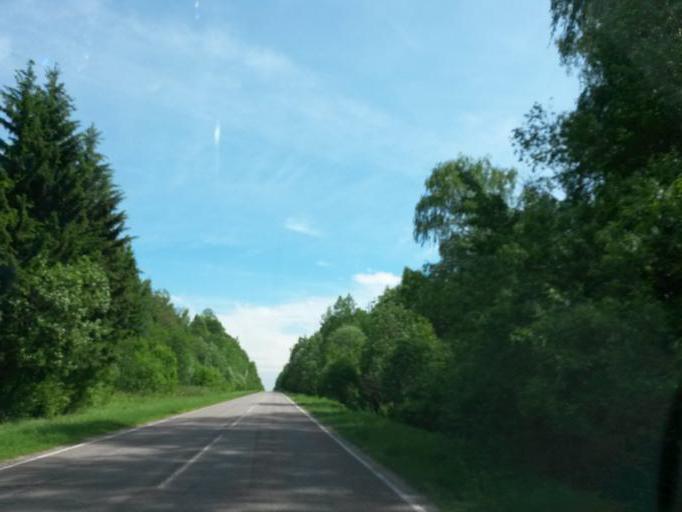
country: RU
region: Moskovskaya
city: Melikhovo
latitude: 55.2245
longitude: 37.6583
